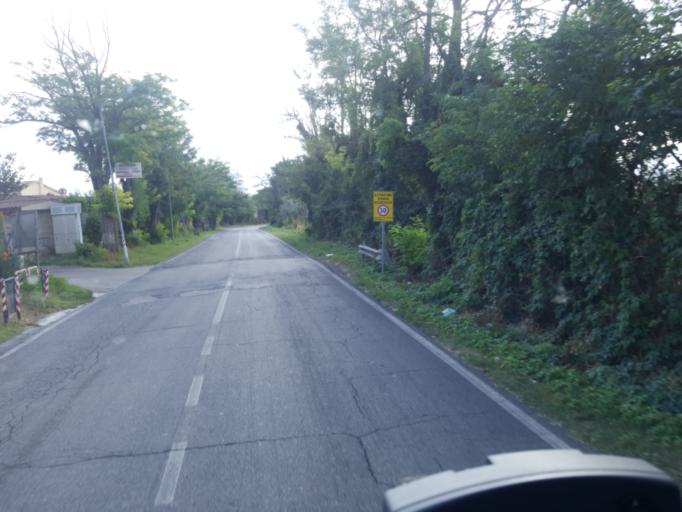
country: IT
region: Latium
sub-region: Citta metropolitana di Roma Capitale
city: Bivio di Capanelle
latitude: 42.1239
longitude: 12.5803
